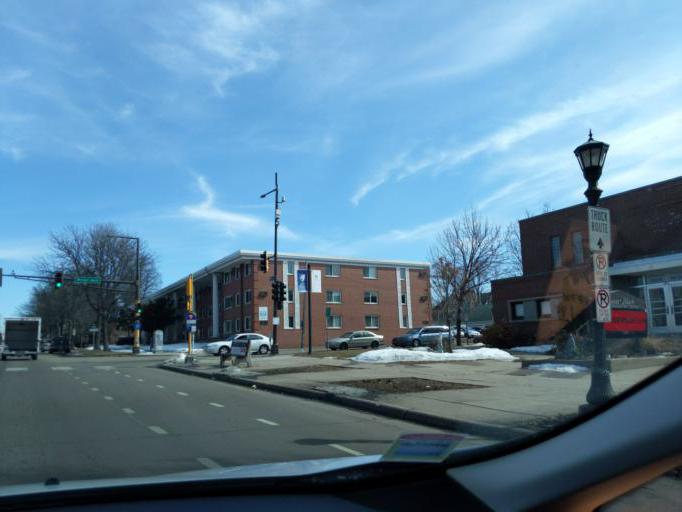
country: US
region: Minnesota
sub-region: Ramsey County
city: Falcon Heights
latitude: 44.9484
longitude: -93.1832
